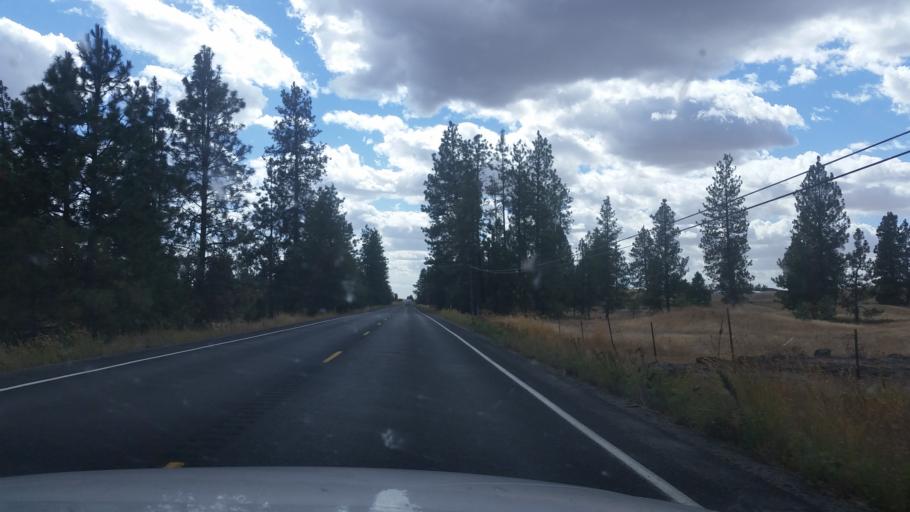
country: US
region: Washington
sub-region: Spokane County
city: Medical Lake
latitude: 47.5417
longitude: -117.7063
